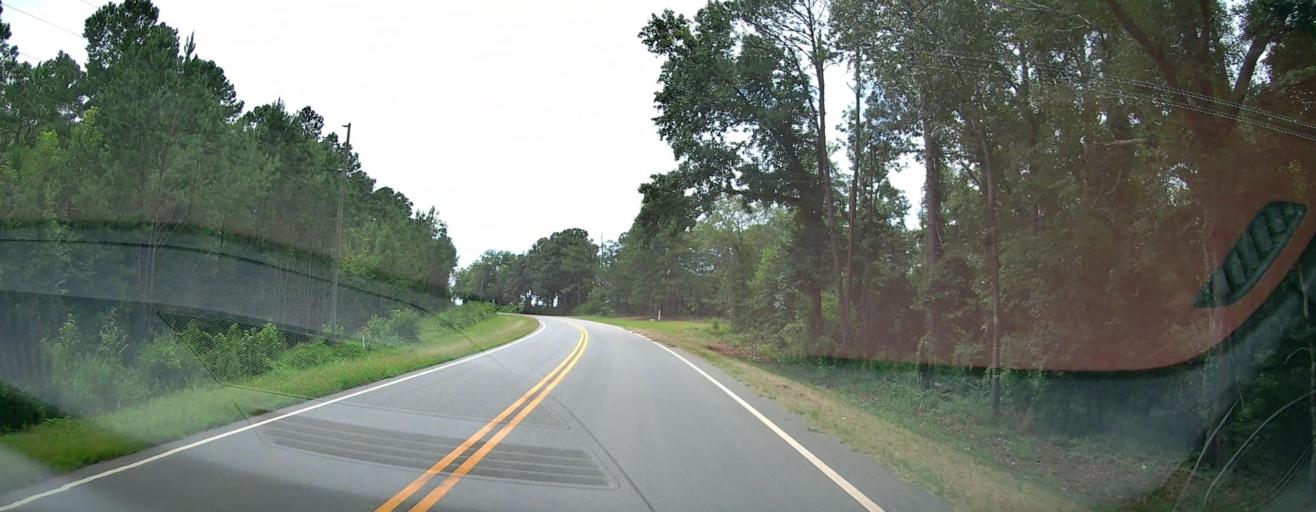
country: US
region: Georgia
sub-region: Macon County
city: Oglethorpe
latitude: 32.2840
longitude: -84.1614
